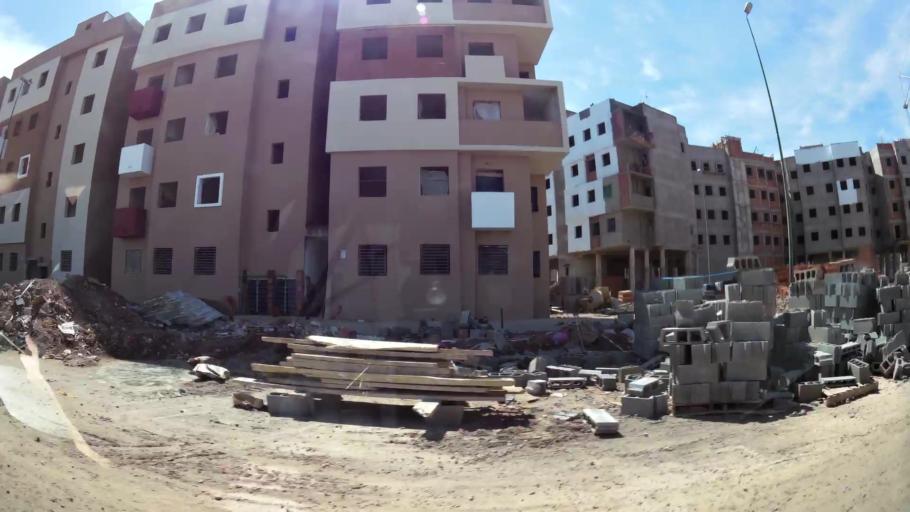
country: MA
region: Marrakech-Tensift-Al Haouz
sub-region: Marrakech
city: Marrakesh
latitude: 31.6328
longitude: -8.0732
